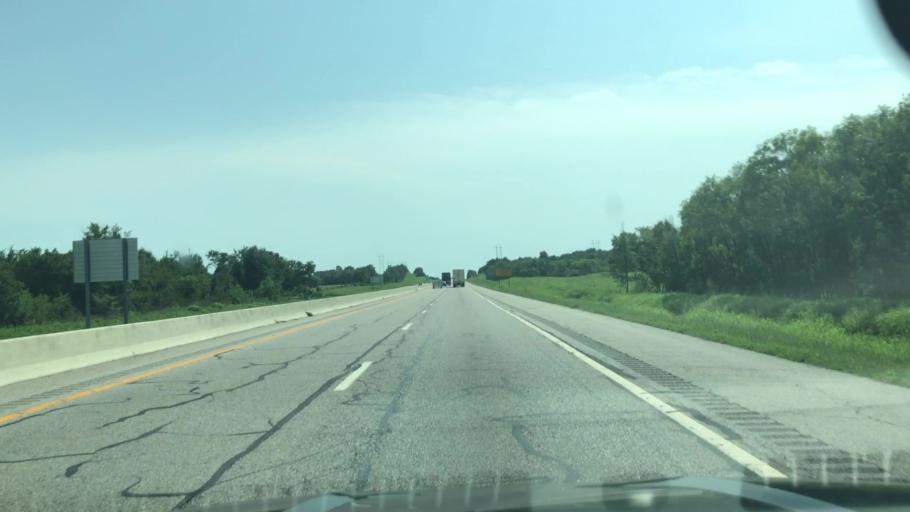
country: US
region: Oklahoma
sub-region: Ottawa County
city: Miami
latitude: 36.8440
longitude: -94.8600
